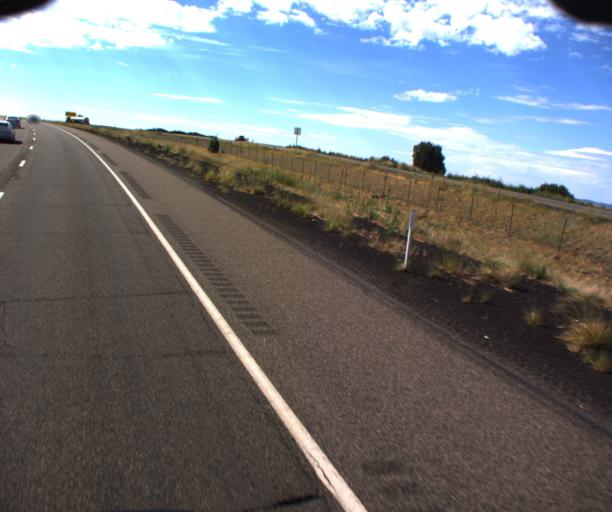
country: US
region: Arizona
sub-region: Yavapai County
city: Village of Oak Creek (Big Park)
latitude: 34.8138
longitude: -111.6116
